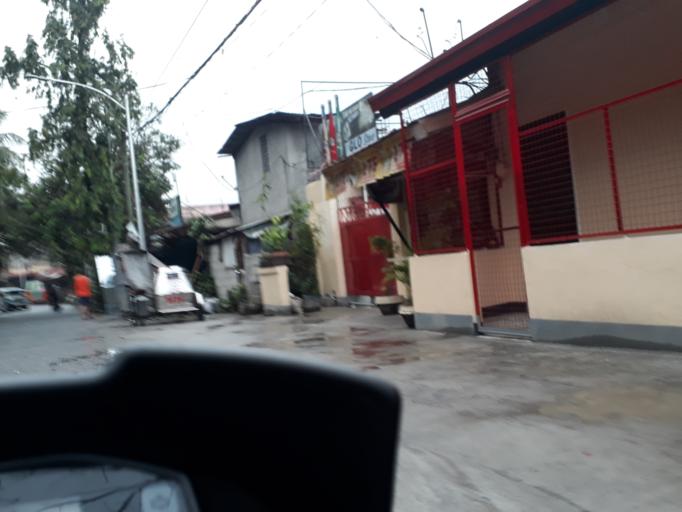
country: PH
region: Central Luzon
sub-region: Province of Bulacan
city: San Jose del Monte
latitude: 14.7702
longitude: 121.0531
